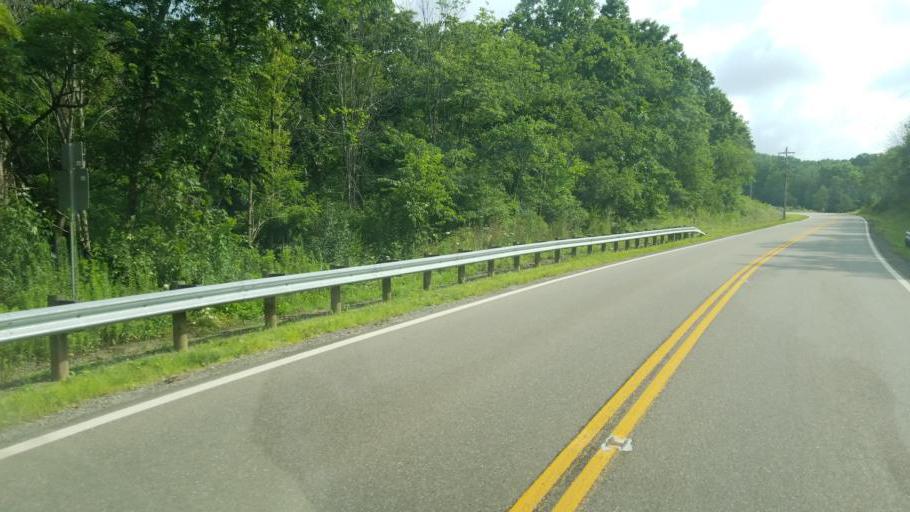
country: US
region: Ohio
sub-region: Columbiana County
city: Salineville
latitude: 40.5280
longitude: -80.8825
